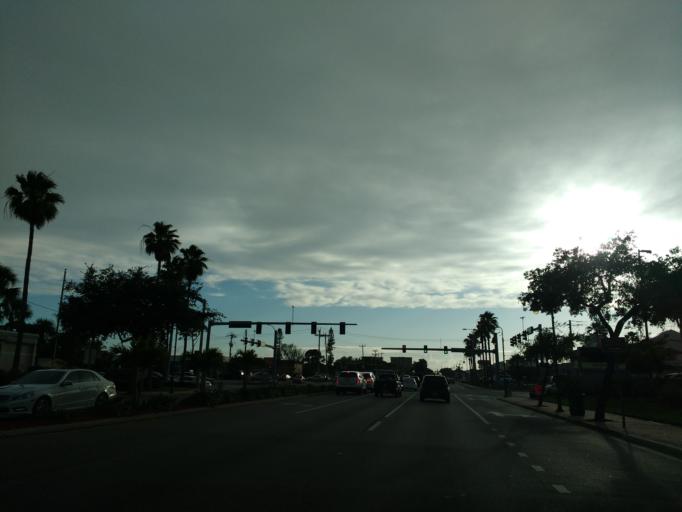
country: US
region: Florida
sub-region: Lee County
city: Cape Coral
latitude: 26.5628
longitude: -81.9572
